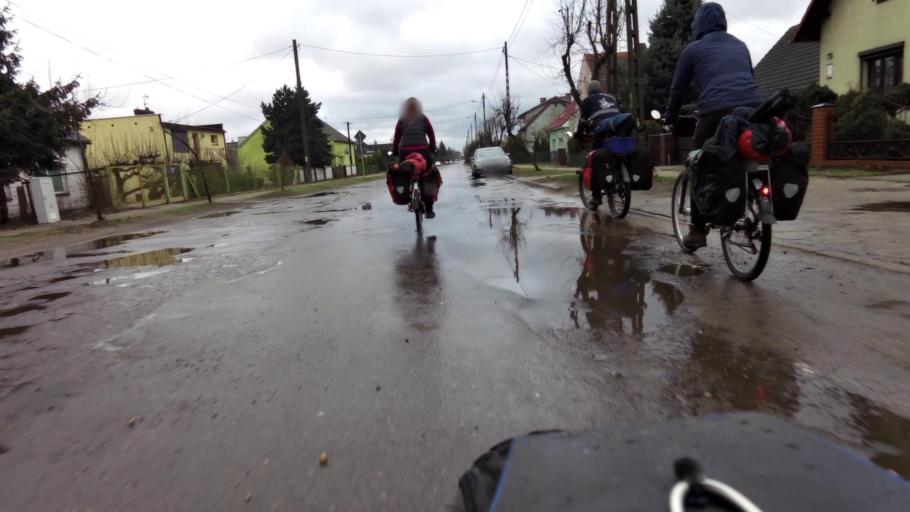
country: PL
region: Lubusz
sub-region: Powiat gorzowski
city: Witnica
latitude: 52.6820
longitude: 14.8901
